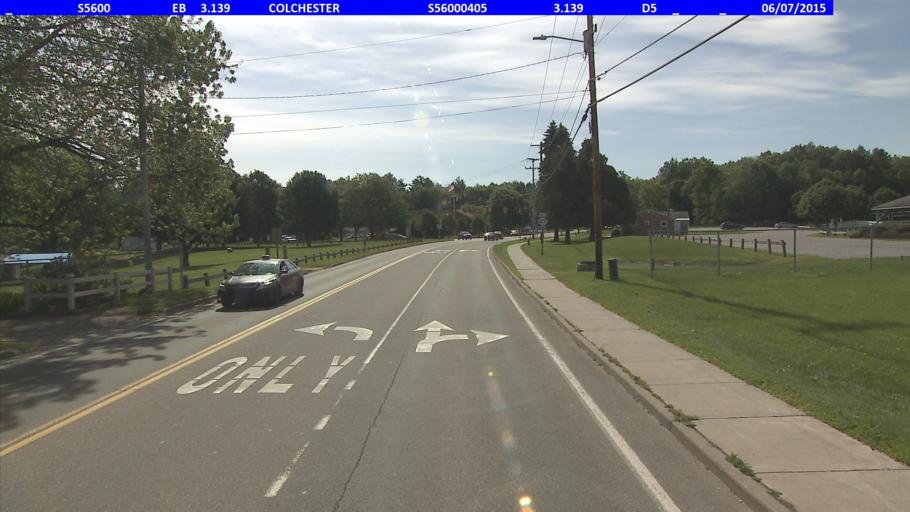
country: US
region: Vermont
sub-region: Chittenden County
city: Winooski
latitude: 44.5451
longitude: -73.2168
